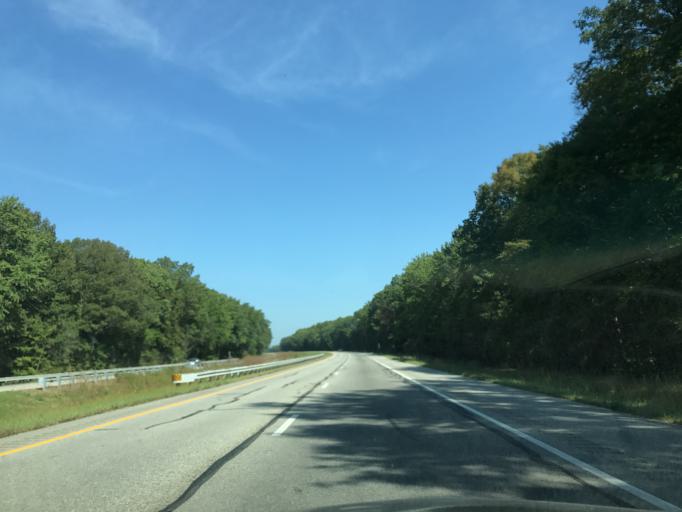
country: US
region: Delaware
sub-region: New Castle County
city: Townsend
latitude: 39.2801
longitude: -75.8578
